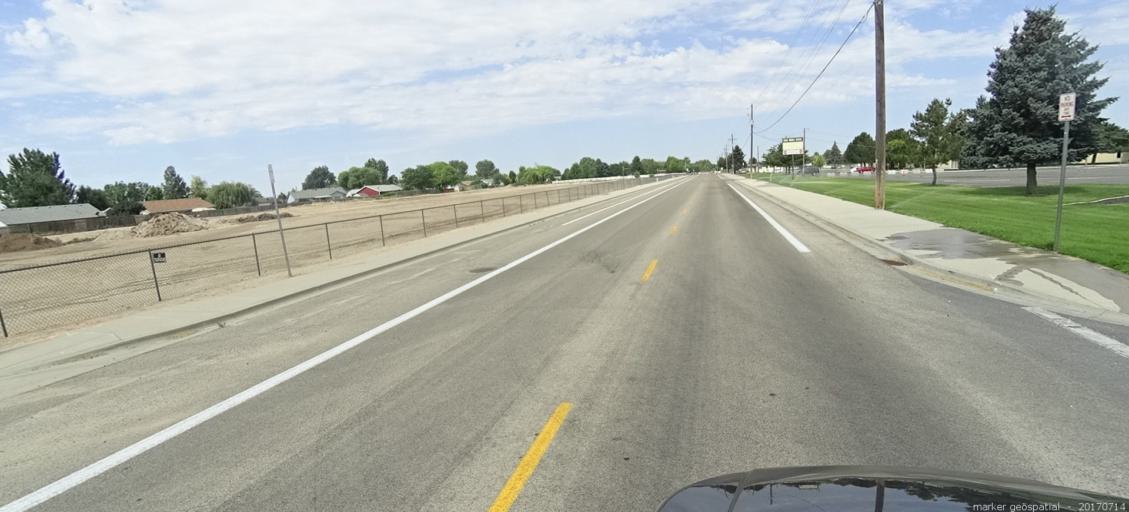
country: US
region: Idaho
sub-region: Ada County
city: Kuna
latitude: 43.4957
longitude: -116.4286
